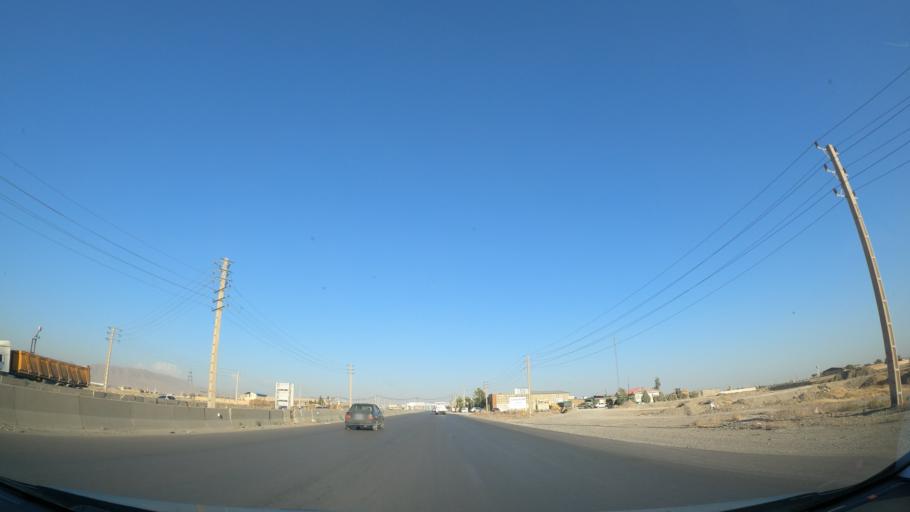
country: IR
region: Alborz
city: Hashtgerd
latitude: 35.9196
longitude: 50.7494
